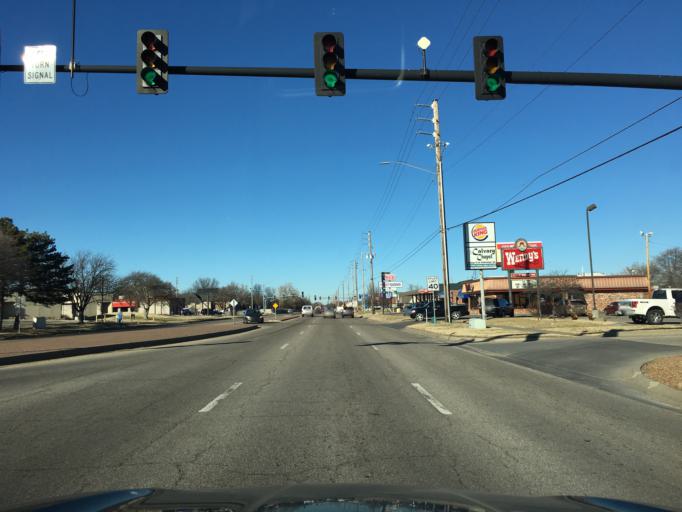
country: US
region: Kansas
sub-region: Sedgwick County
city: Bellaire
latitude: 37.6843
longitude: -97.2444
